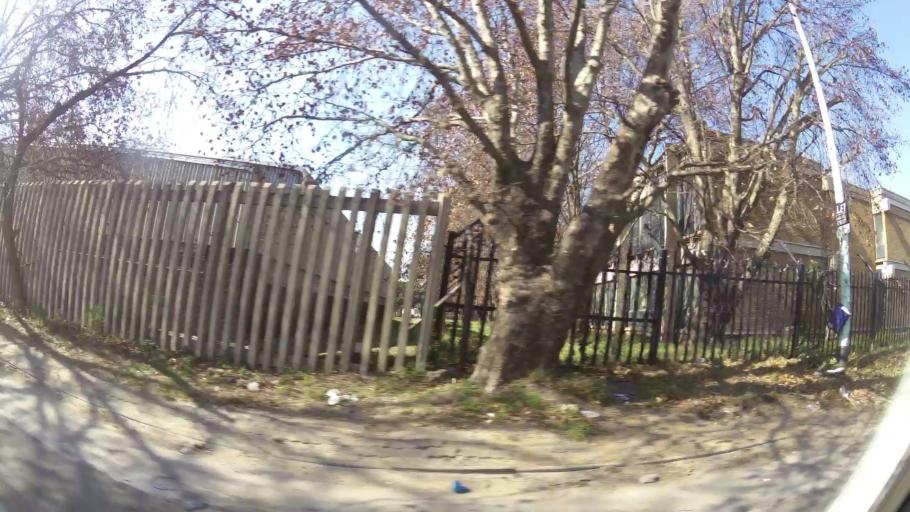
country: ZA
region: Gauteng
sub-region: Ekurhuleni Metropolitan Municipality
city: Boksburg
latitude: -26.2166
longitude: 28.2883
